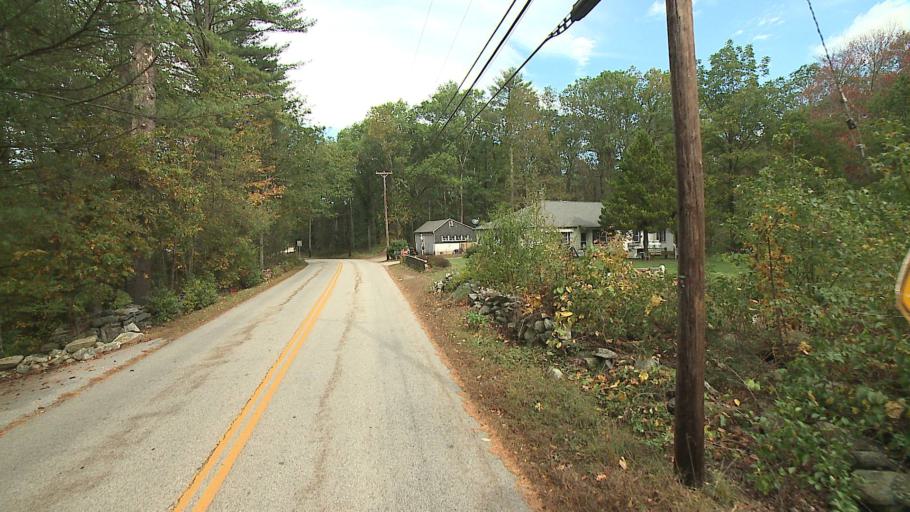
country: US
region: Connecticut
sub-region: Windham County
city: Thompson
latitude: 41.9408
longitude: -71.8203
